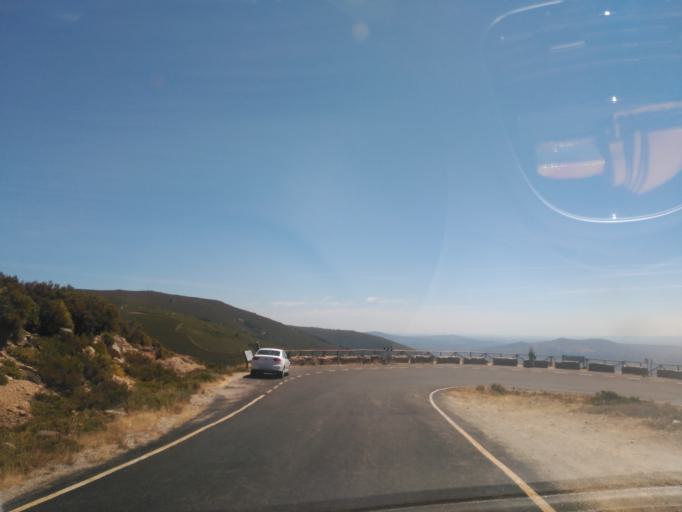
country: ES
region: Castille and Leon
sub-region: Provincia de Zamora
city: Trefacio
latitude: 42.1553
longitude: -6.7202
